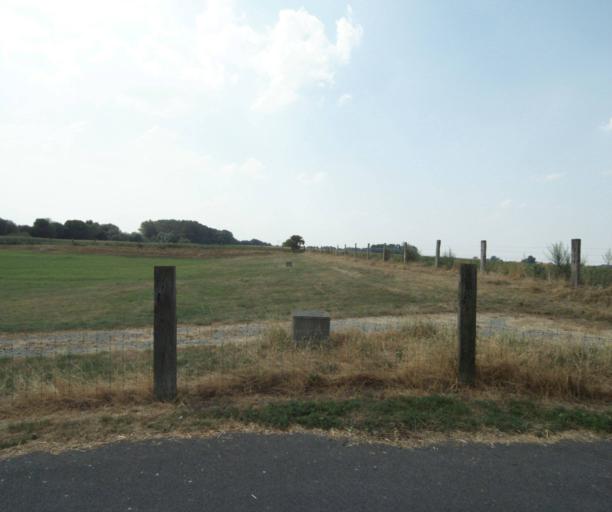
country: FR
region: Nord-Pas-de-Calais
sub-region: Departement du Nord
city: Quesnoy-sur-Deule
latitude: 50.7189
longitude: 2.9812
